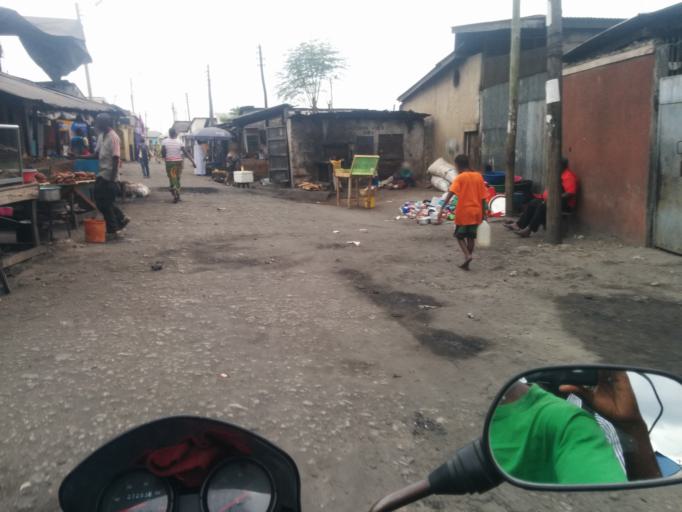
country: TZ
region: Dar es Salaam
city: Dar es Salaam
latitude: -6.8369
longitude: 39.2784
